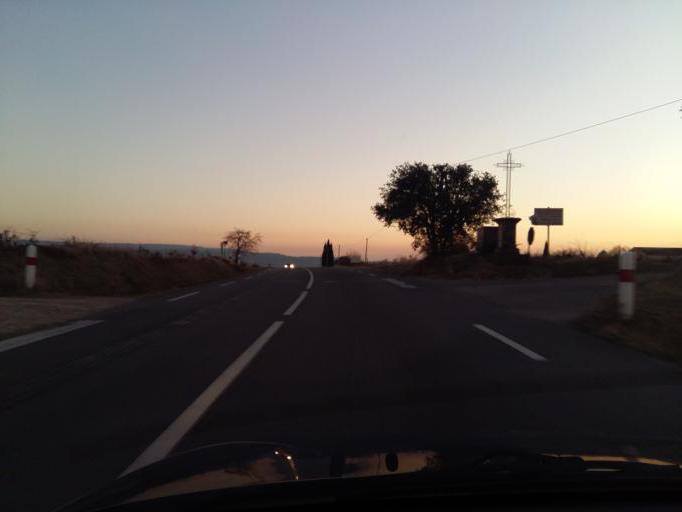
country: FR
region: Rhone-Alpes
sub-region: Departement de la Drome
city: Tulette
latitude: 44.2925
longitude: 4.9426
